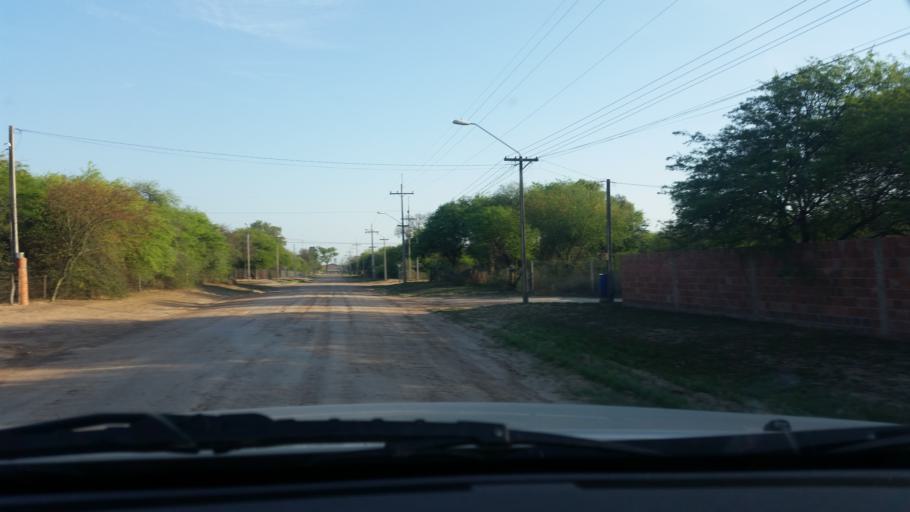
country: PY
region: Boqueron
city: Filadelfia
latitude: -22.3434
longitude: -60.0388
